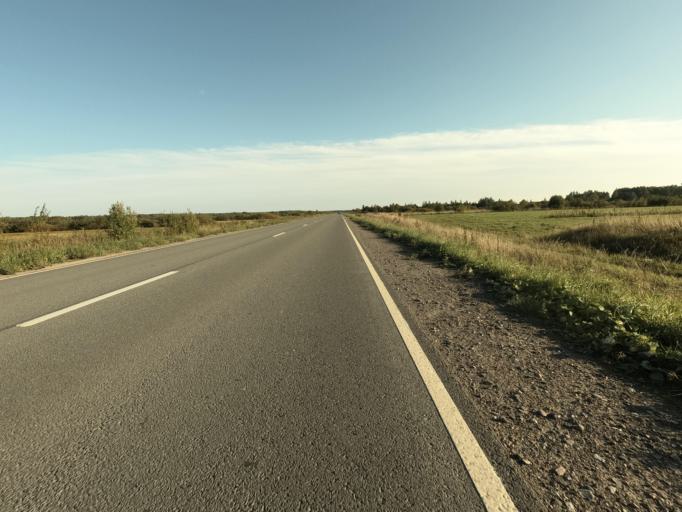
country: RU
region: St.-Petersburg
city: Sapernyy
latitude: 59.7491
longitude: 30.6401
